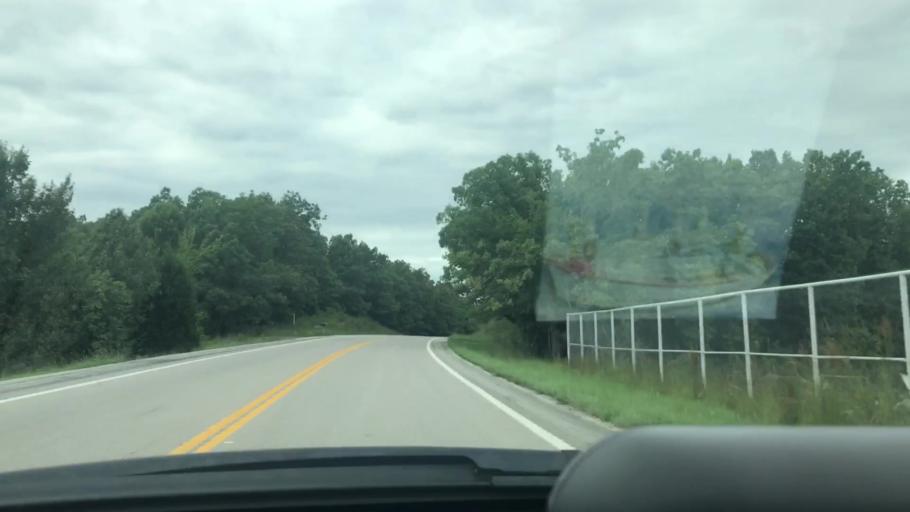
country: US
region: Missouri
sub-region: Benton County
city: Warsaw
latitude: 38.1649
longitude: -93.3071
